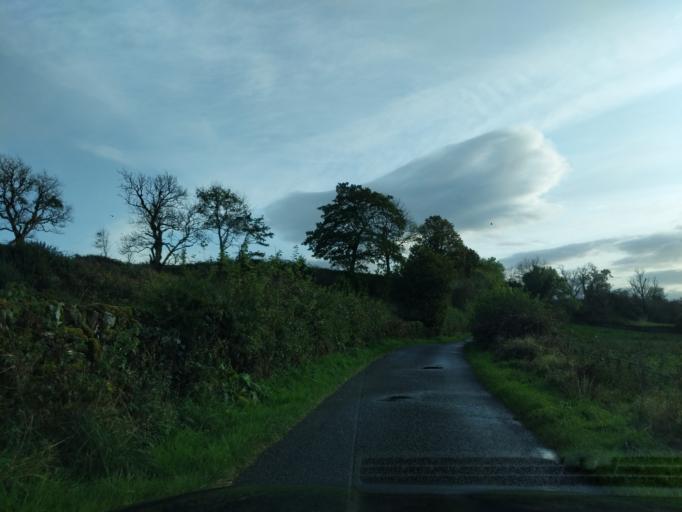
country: GB
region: Scotland
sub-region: Dumfries and Galloway
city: Kirkcudbright
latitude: 54.8410
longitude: -4.1800
